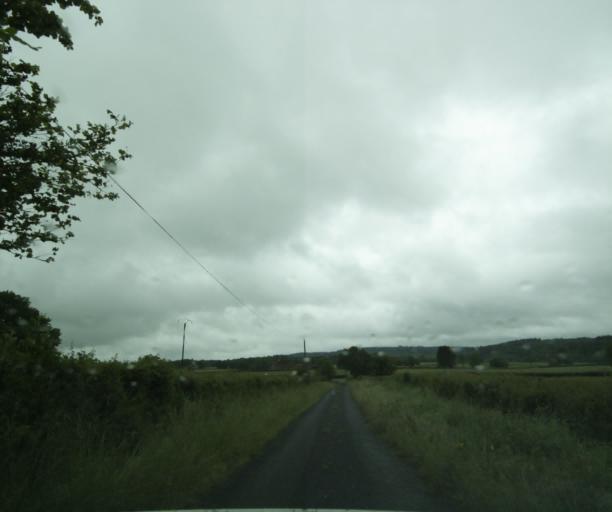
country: FR
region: Bourgogne
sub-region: Departement de Saone-et-Loire
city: Saint-Vallier
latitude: 46.5181
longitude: 4.3892
